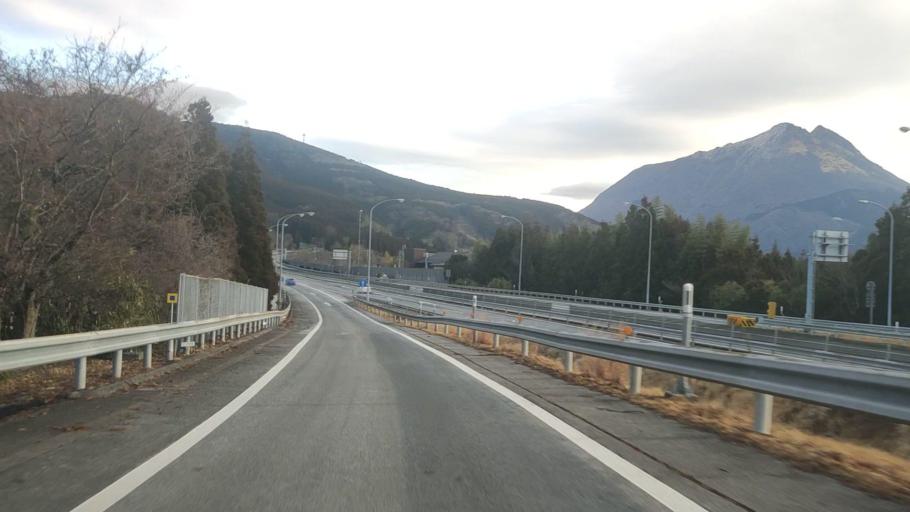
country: JP
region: Oita
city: Beppu
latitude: 33.2584
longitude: 131.3298
